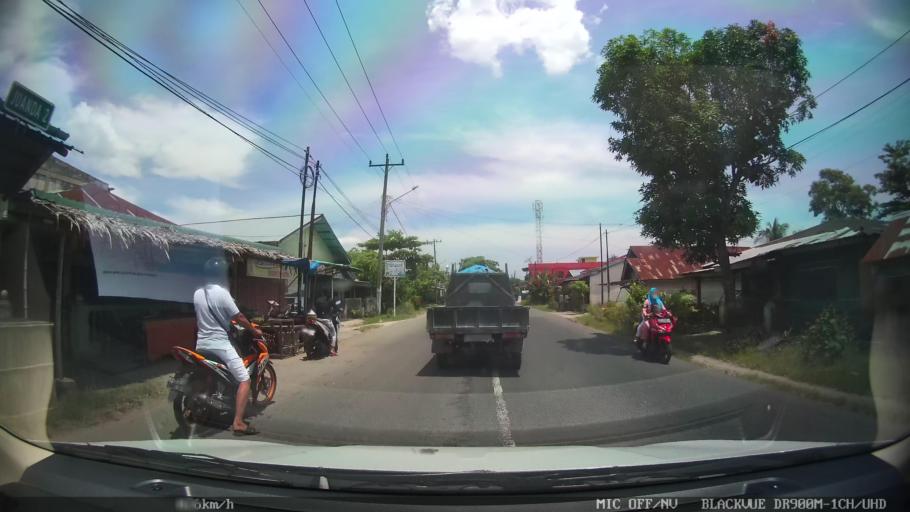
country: ID
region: North Sumatra
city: Binjai
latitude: 3.6016
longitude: 98.4963
